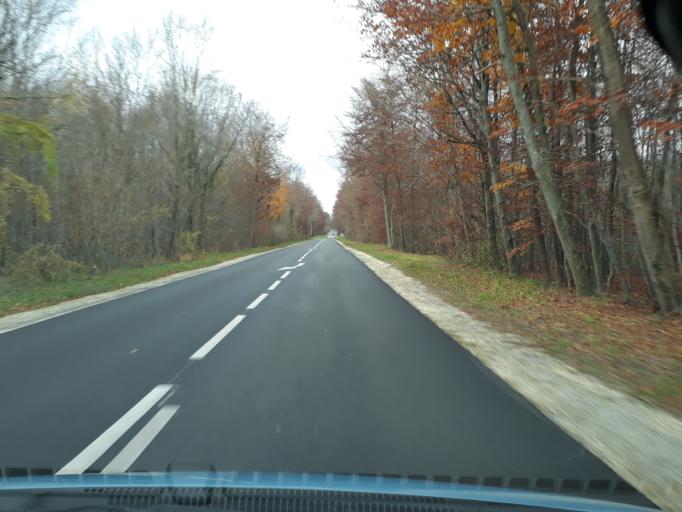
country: FR
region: Ile-de-France
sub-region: Departement de Seine-et-Marne
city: Thomery
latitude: 48.3950
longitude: 2.7673
